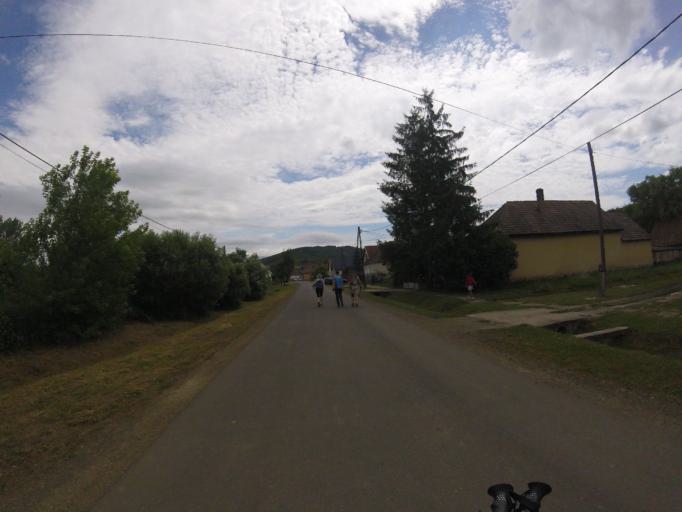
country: HU
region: Nograd
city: Romhany
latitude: 47.9191
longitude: 19.2584
